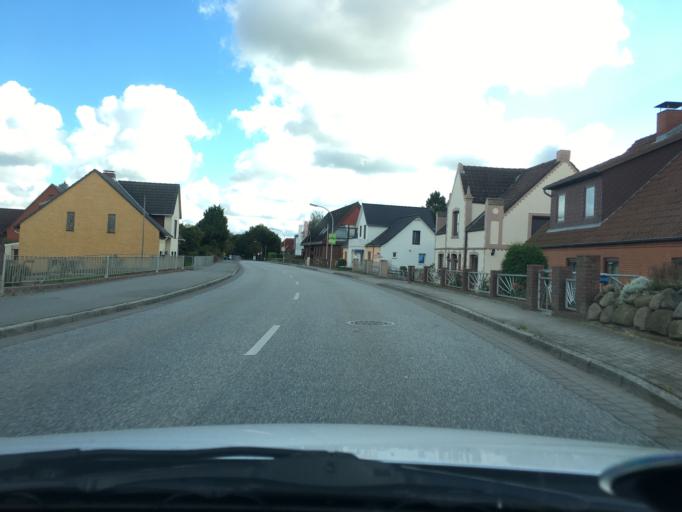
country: DE
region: Schleswig-Holstein
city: Barsbek
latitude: 54.4047
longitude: 10.3292
